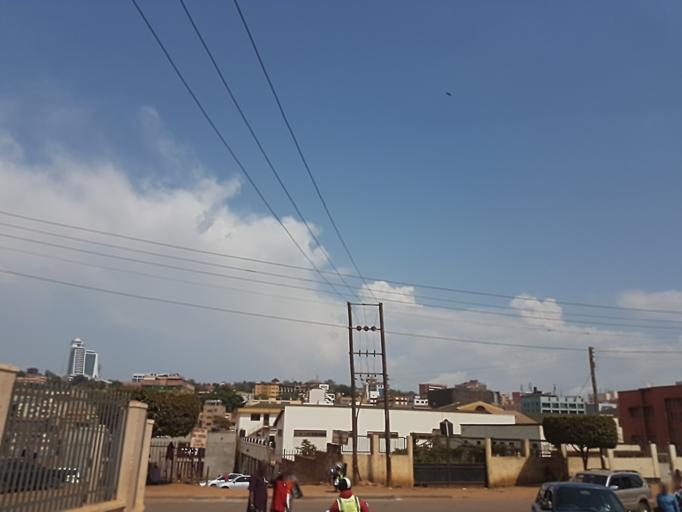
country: UG
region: Central Region
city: Kampala Central Division
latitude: 0.3180
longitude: 32.5702
